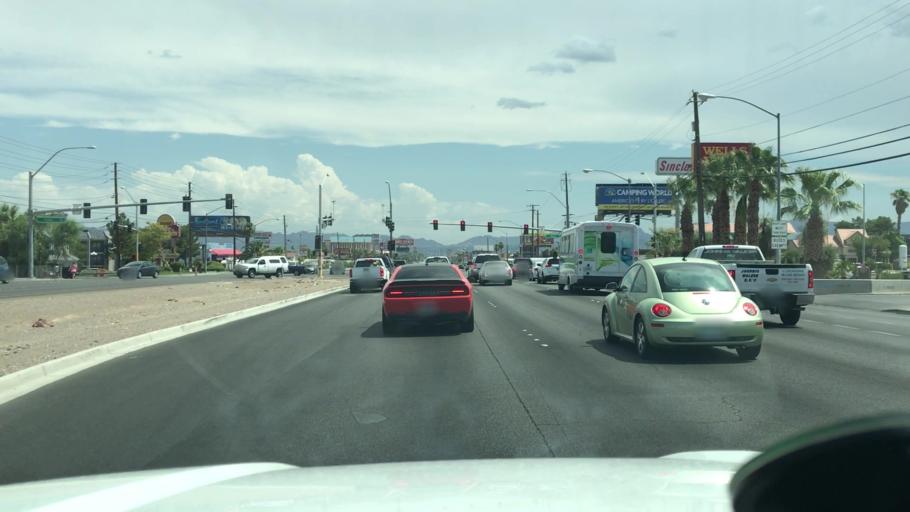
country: US
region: Nevada
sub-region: Clark County
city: Winchester
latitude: 36.1221
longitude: -115.0750
